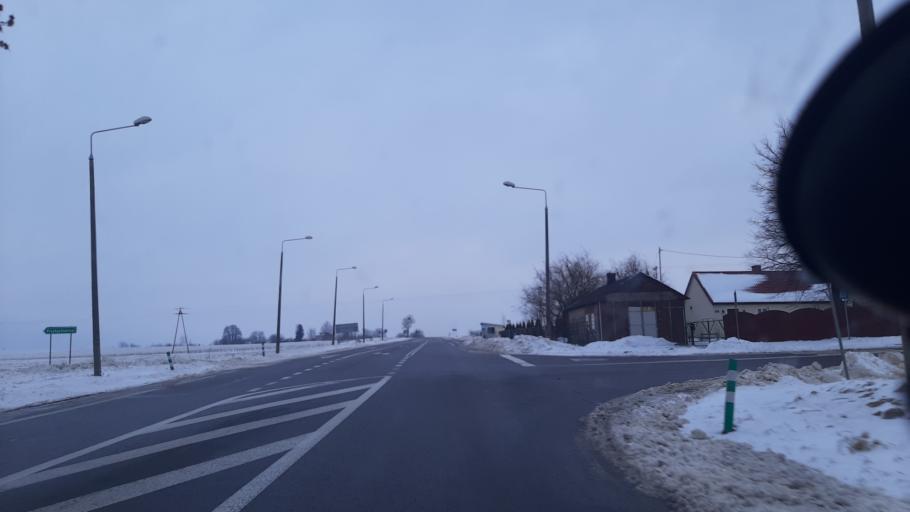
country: PL
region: Lublin Voivodeship
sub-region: Powiat pulawski
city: Markuszow
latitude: 51.3693
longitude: 22.2808
